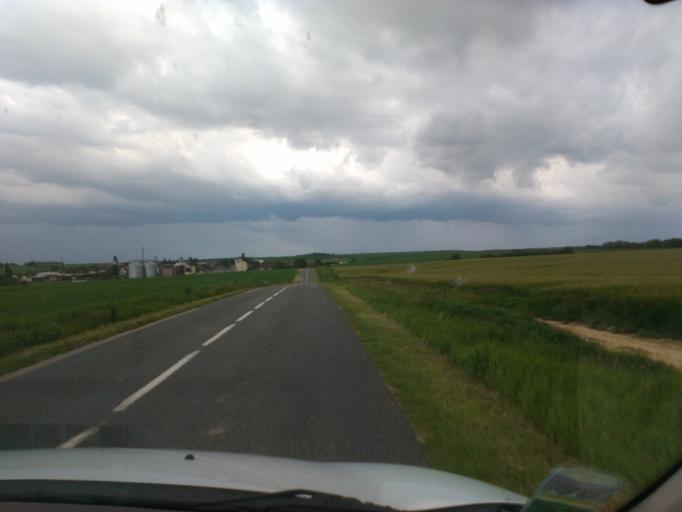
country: FR
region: Bourgogne
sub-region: Departement de l'Yonne
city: Thorigny-sur-Oreuse
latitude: 48.3521
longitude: 3.3931
